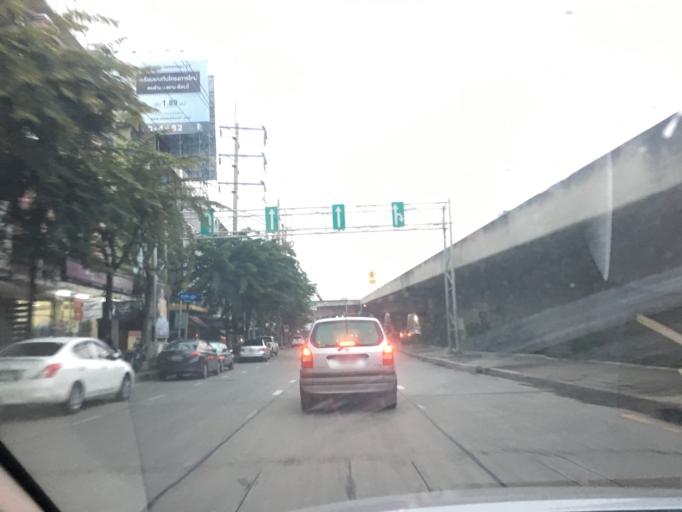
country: TH
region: Bangkok
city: Bang Kho Laem
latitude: 13.6958
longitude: 100.4983
